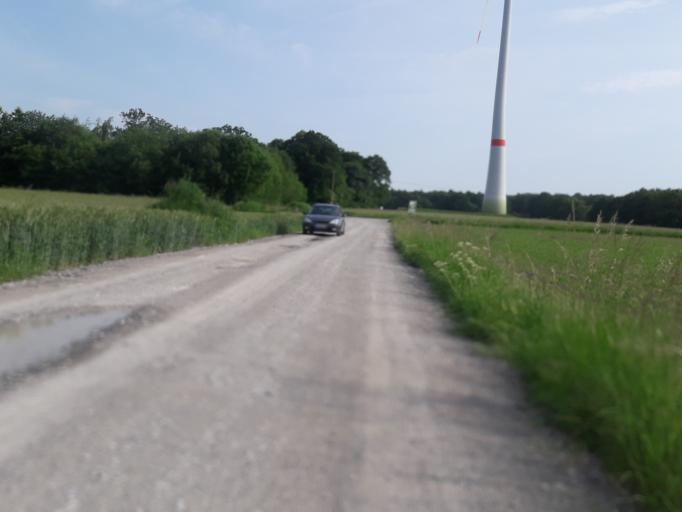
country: DE
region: North Rhine-Westphalia
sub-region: Regierungsbezirk Detmold
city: Salzkotten
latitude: 51.6961
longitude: 8.6465
